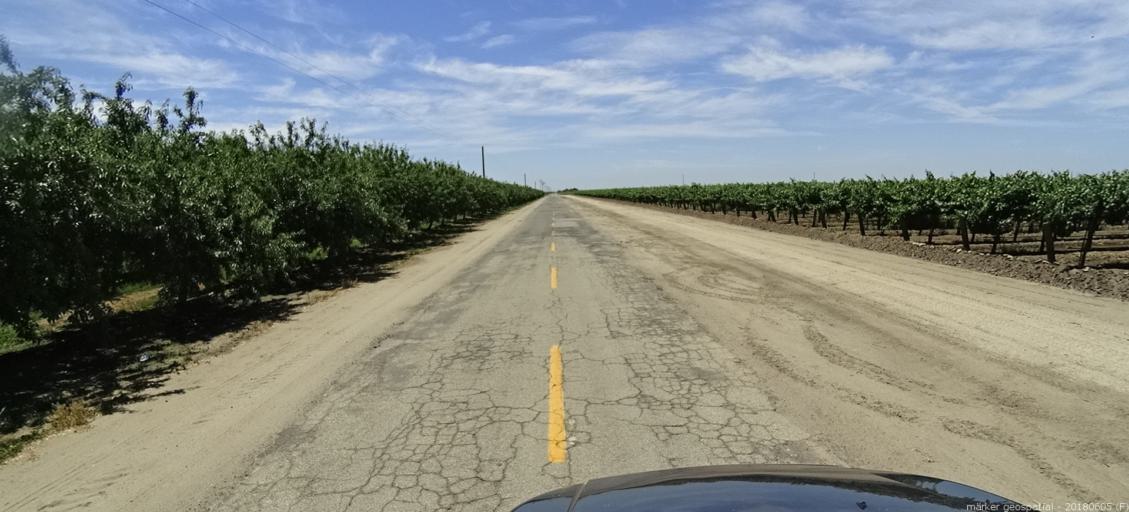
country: US
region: California
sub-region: Madera County
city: Chowchilla
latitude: 37.0906
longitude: -120.3611
